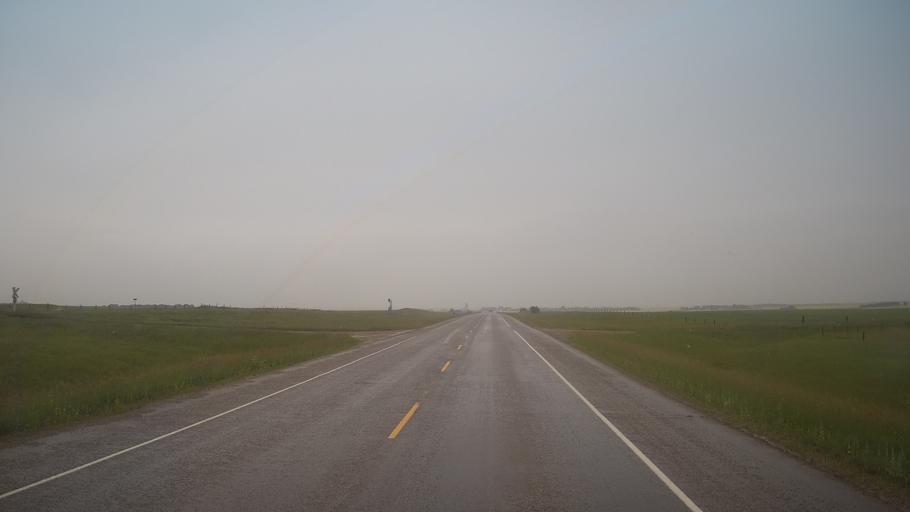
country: CA
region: Saskatchewan
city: Wilkie
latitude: 52.1877
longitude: -108.4064
